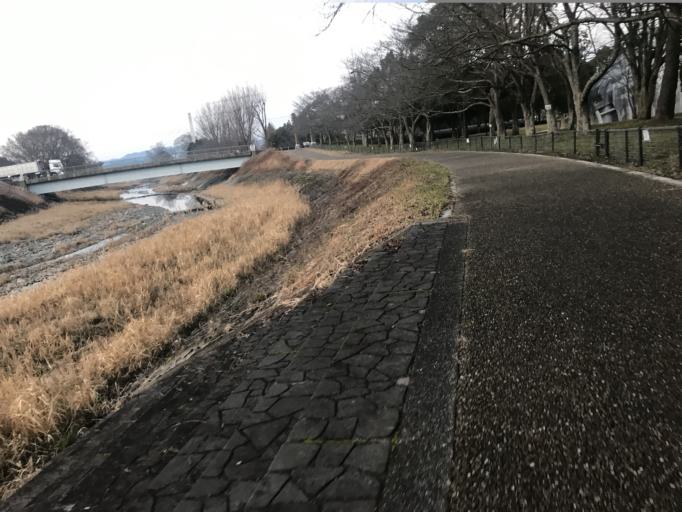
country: JP
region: Kyoto
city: Kameoka
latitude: 35.0121
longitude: 135.5499
